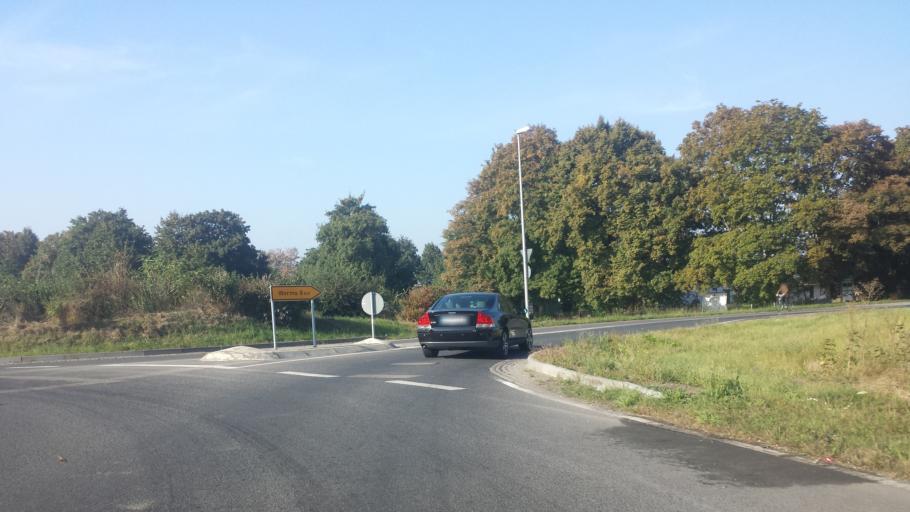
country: DE
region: Hesse
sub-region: Regierungsbezirk Darmstadt
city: Burstadt
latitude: 49.6221
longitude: 8.4266
